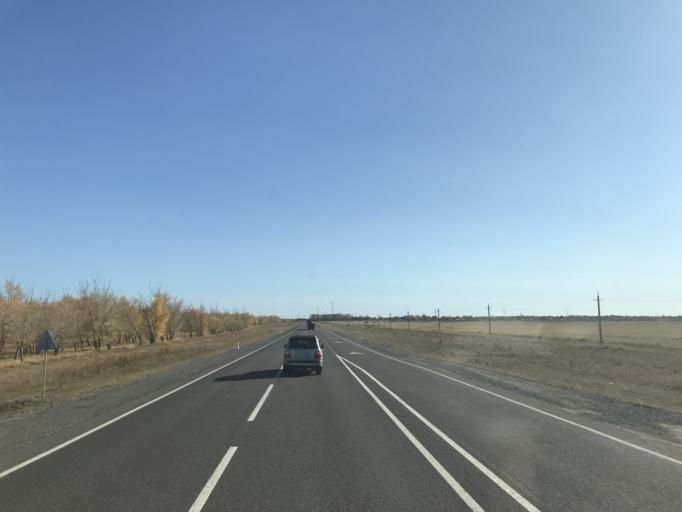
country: KZ
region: Pavlodar
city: Aksu
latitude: 51.9395
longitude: 77.3205
